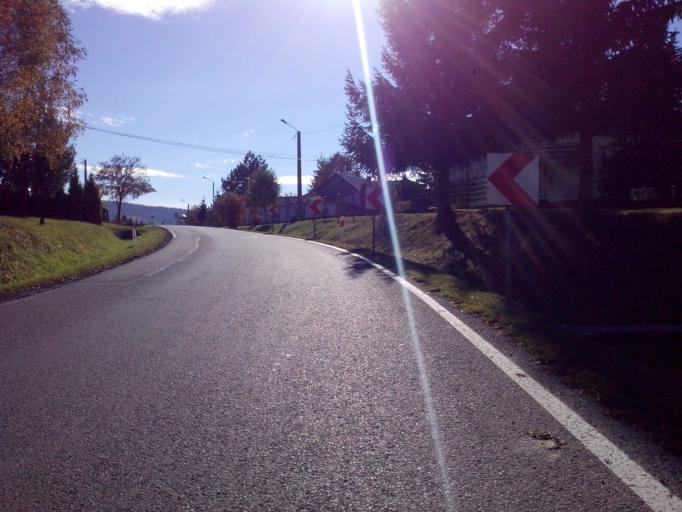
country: PL
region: Subcarpathian Voivodeship
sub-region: Powiat strzyzowski
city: Jawornik
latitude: 49.7931
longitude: 21.8588
